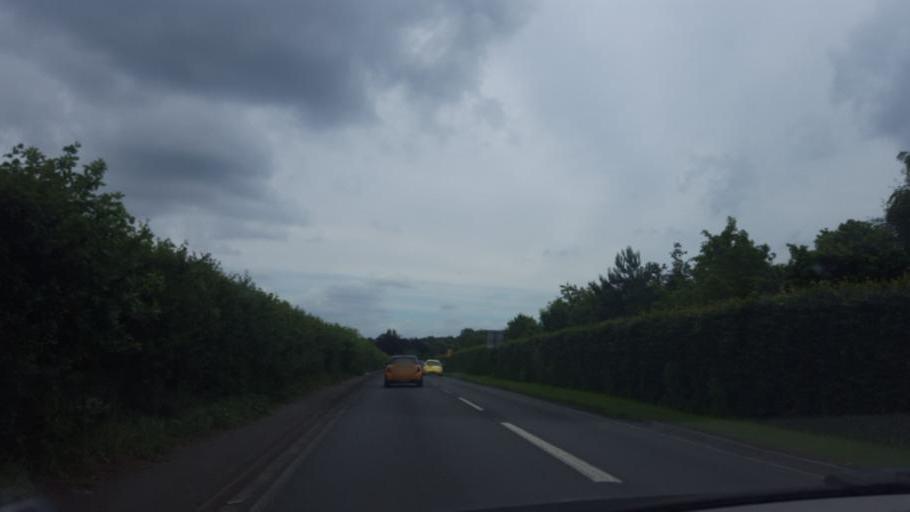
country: GB
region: England
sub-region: Royal Borough of Windsor and Maidenhead
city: Hurley
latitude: 51.5416
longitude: -0.8196
